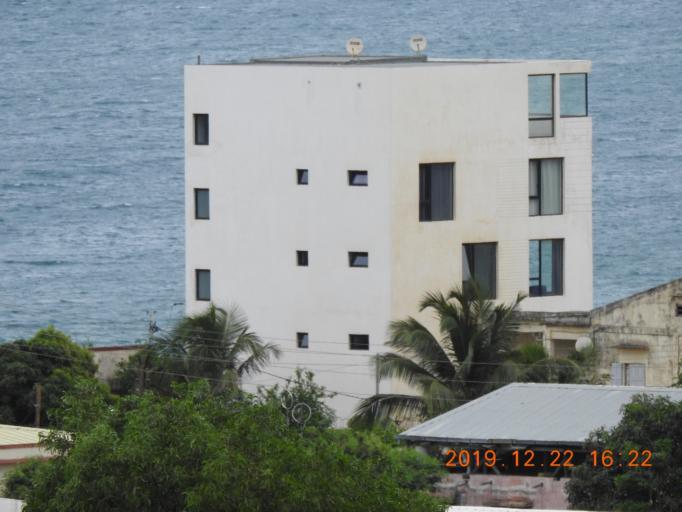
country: MG
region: Diana
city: Antsiranana
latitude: -12.2691
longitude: 49.2918
